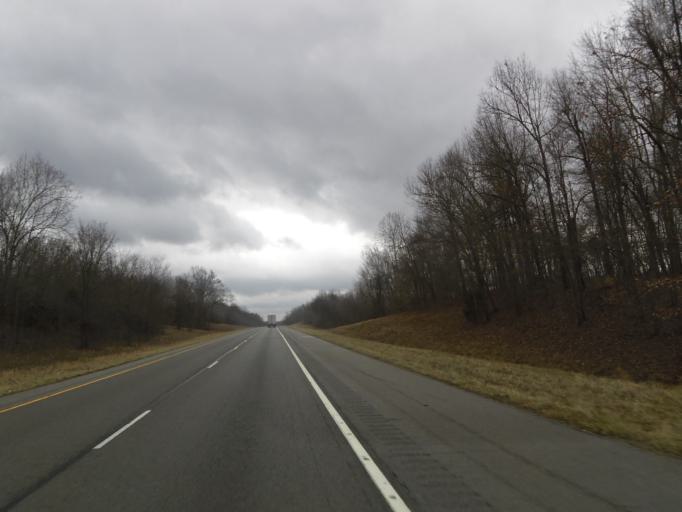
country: US
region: Illinois
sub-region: Massac County
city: Metropolis
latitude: 37.2625
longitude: -88.7331
